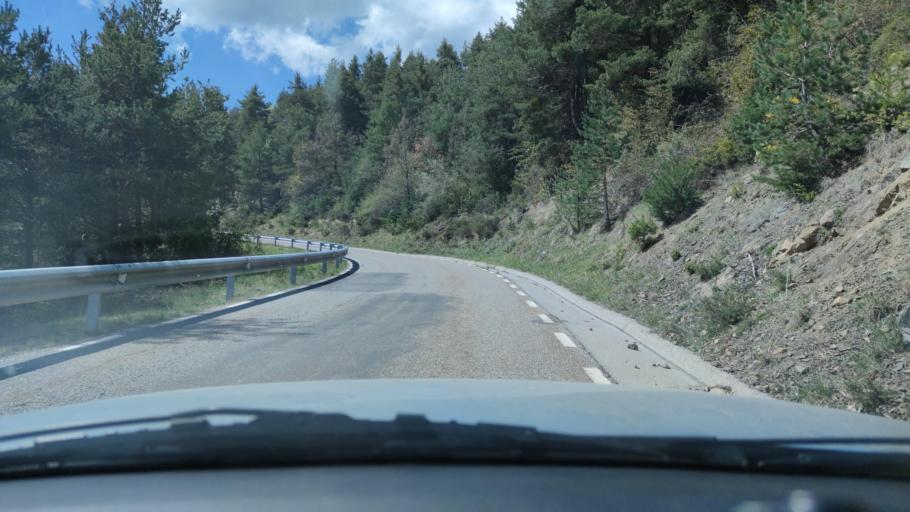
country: ES
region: Catalonia
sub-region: Provincia de Lleida
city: Coll de Nargo
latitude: 42.2915
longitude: 1.2465
